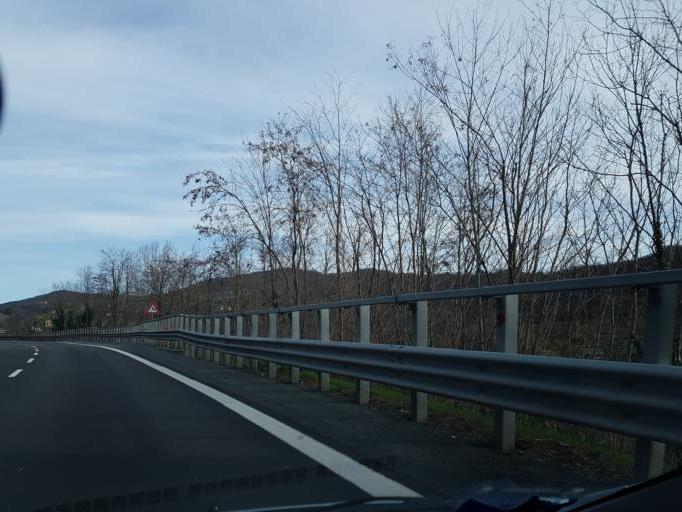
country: IT
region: Liguria
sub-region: Provincia di Genova
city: Serra Ricco
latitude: 44.5194
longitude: 8.9362
